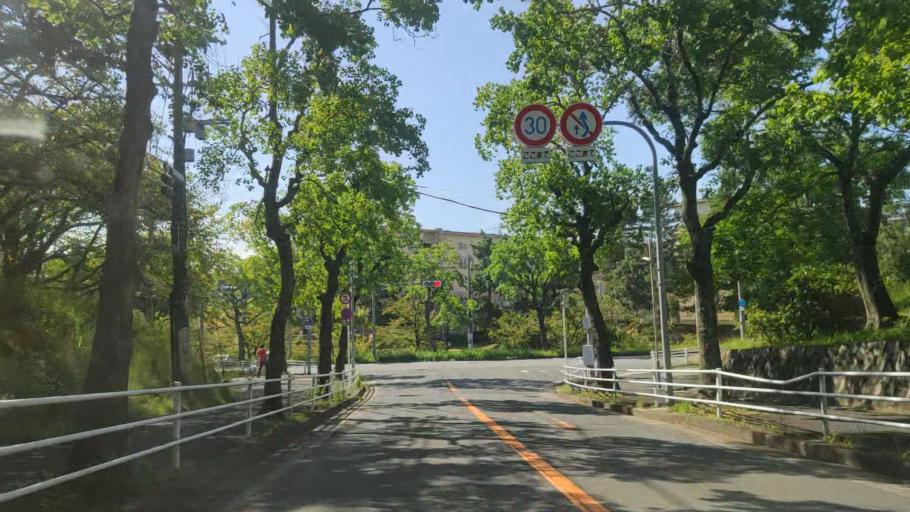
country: JP
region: Osaka
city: Mino
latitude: 34.8221
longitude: 135.5073
